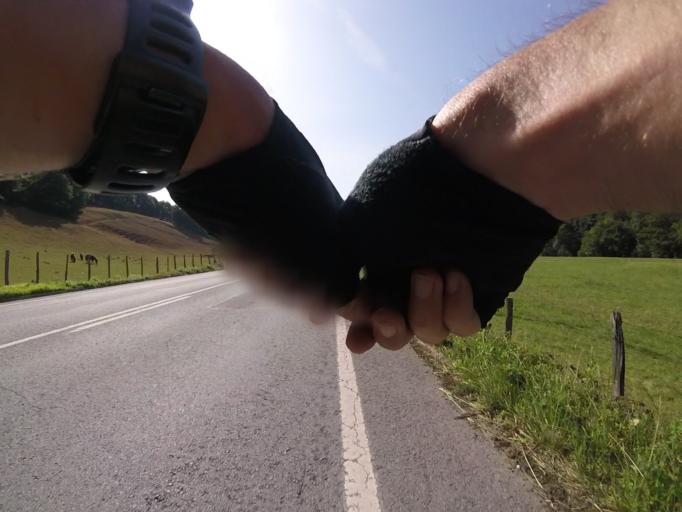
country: ES
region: Navarre
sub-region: Provincia de Navarra
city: Zugarramurdi
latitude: 43.1713
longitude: -1.4930
